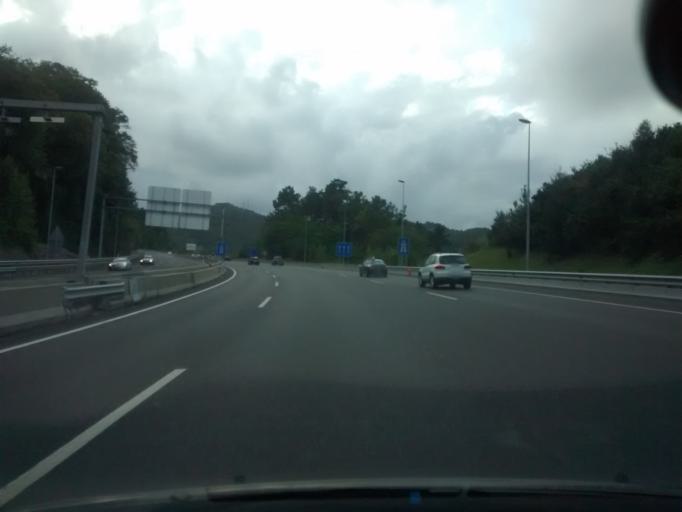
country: ES
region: Basque Country
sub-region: Provincia de Guipuzcoa
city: Usurbil
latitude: 43.2924
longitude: -2.0393
